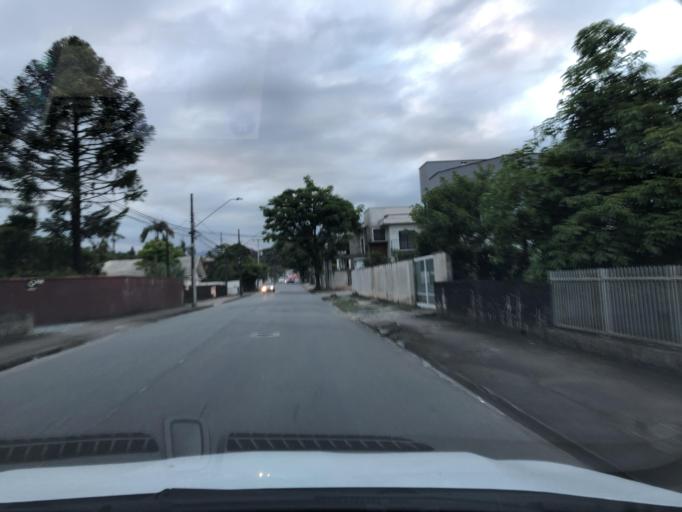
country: BR
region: Santa Catarina
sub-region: Joinville
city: Joinville
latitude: -26.2909
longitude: -48.8733
